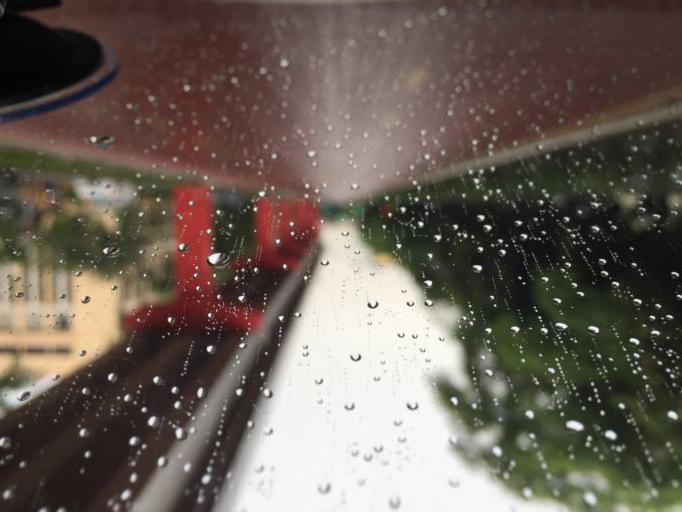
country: MY
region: Selangor
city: Subang Jaya
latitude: 3.0680
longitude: 101.6108
